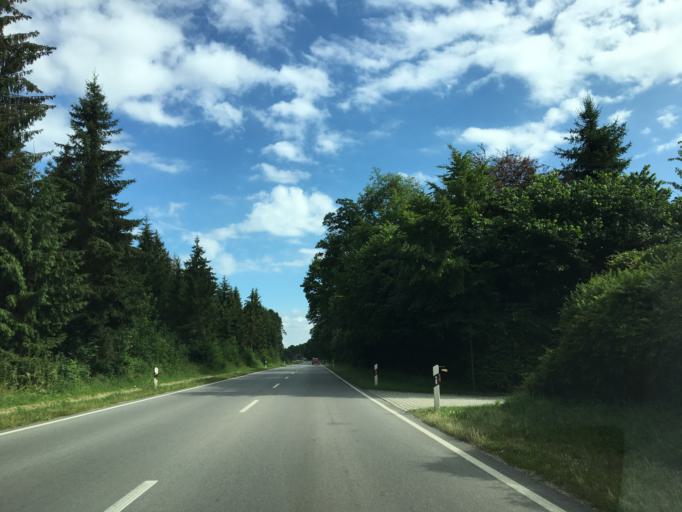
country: DE
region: Bavaria
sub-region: Upper Bavaria
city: Sauerlach
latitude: 47.9599
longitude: 11.6526
